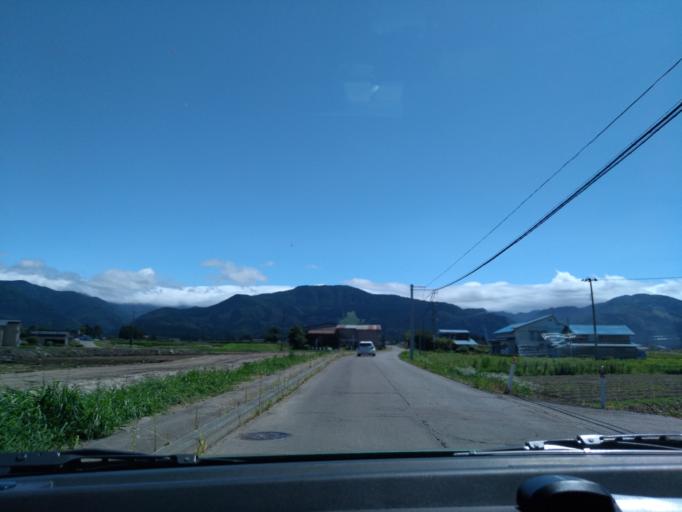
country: JP
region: Akita
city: Kakunodatemachi
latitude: 39.5278
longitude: 140.6119
